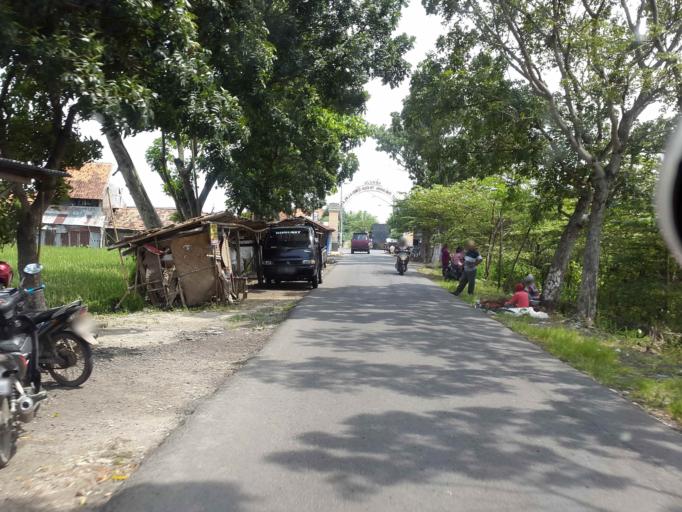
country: ID
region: Central Java
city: Petarukan
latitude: -6.8913
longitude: 109.4449
